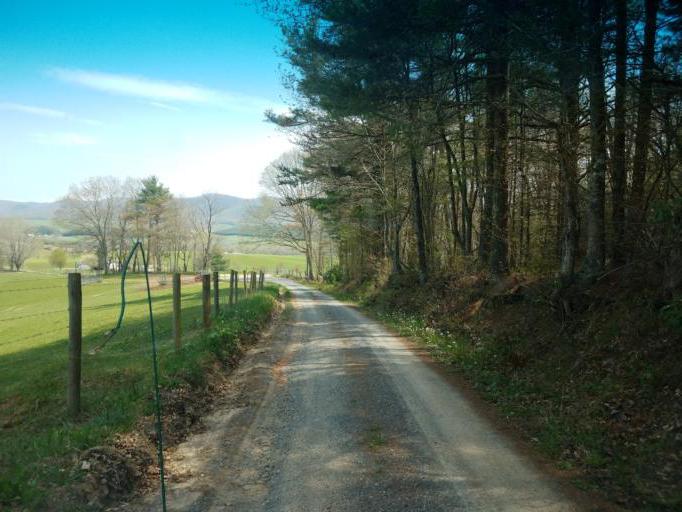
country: US
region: Virginia
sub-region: Smyth County
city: Marion
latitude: 36.7808
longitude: -81.4623
